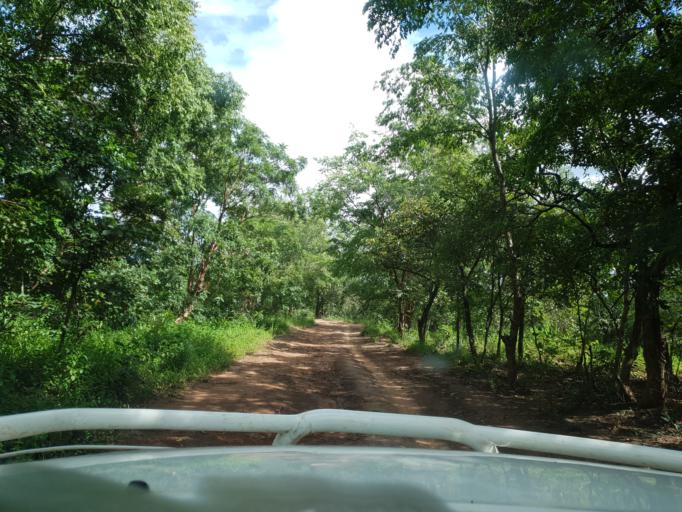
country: CI
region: Savanes
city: Tengrela
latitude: 10.4597
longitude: -6.7960
